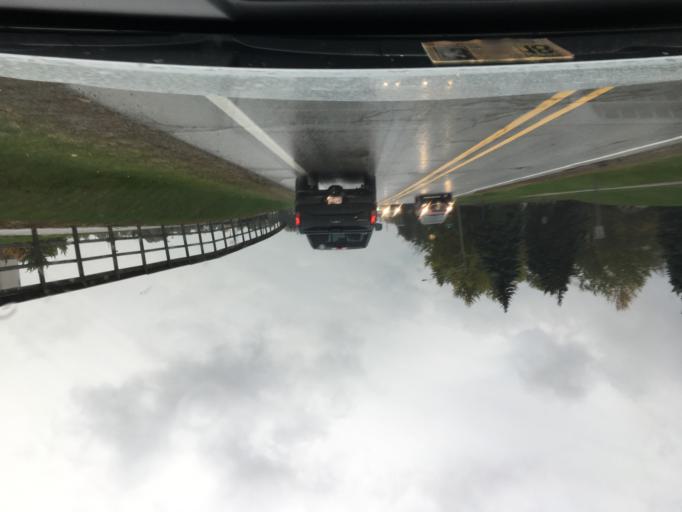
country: US
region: Michigan
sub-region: Oakland County
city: Auburn Hills
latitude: 42.6974
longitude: -83.1948
